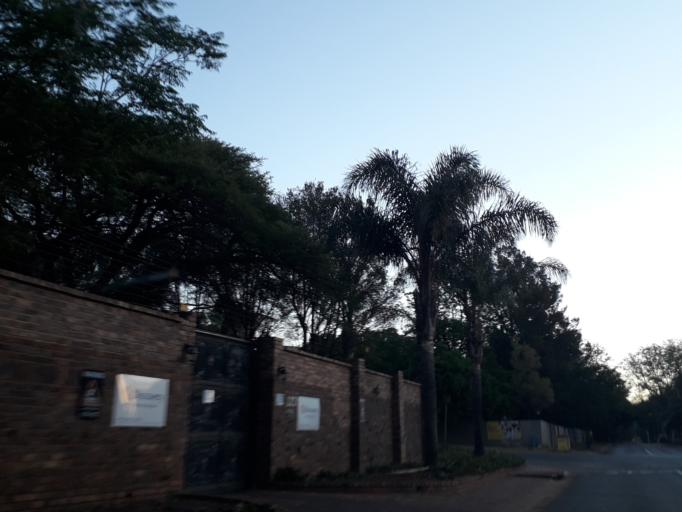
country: ZA
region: Gauteng
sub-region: City of Johannesburg Metropolitan Municipality
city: Roodepoort
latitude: -26.1385
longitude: 27.9374
